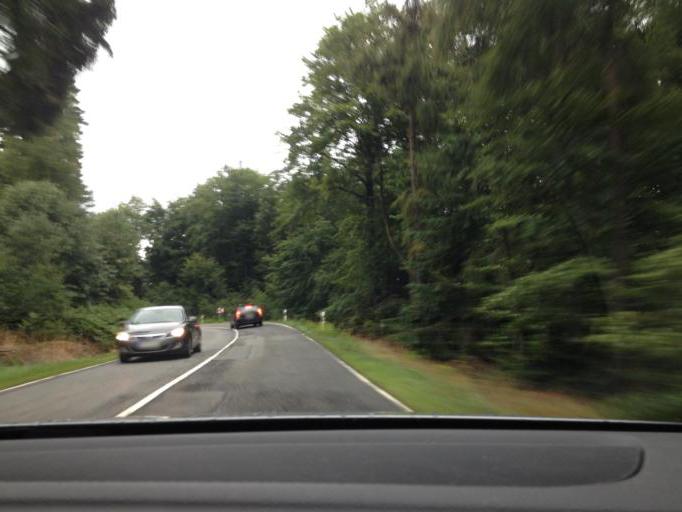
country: DE
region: Hesse
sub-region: Regierungsbezirk Darmstadt
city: Schlangenbad
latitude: 50.1031
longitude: 8.1396
